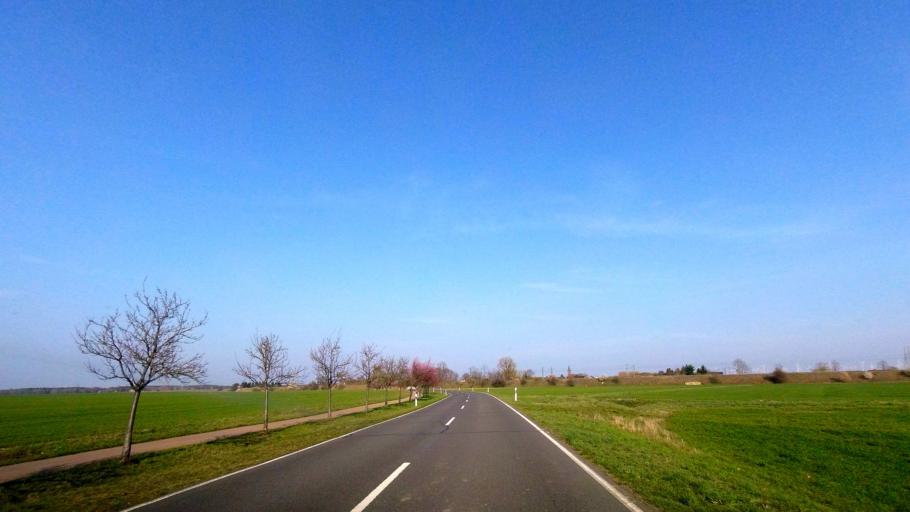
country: DE
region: Brandenburg
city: Juterbog
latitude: 52.0299
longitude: 13.0743
